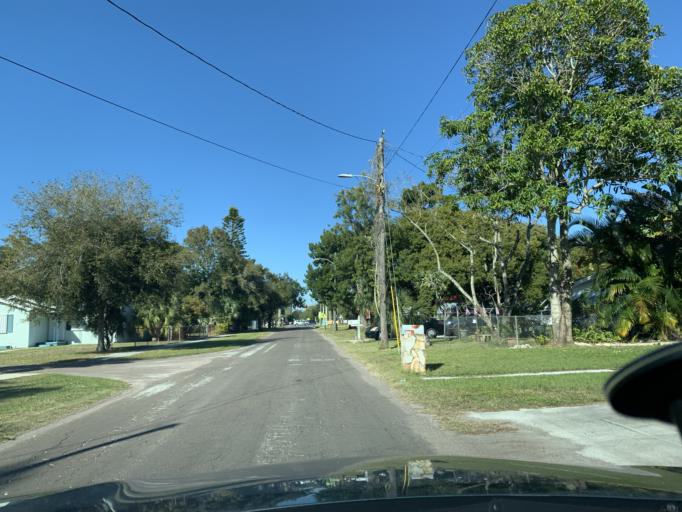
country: US
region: Florida
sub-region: Pinellas County
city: Gulfport
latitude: 27.7469
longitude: -82.7038
